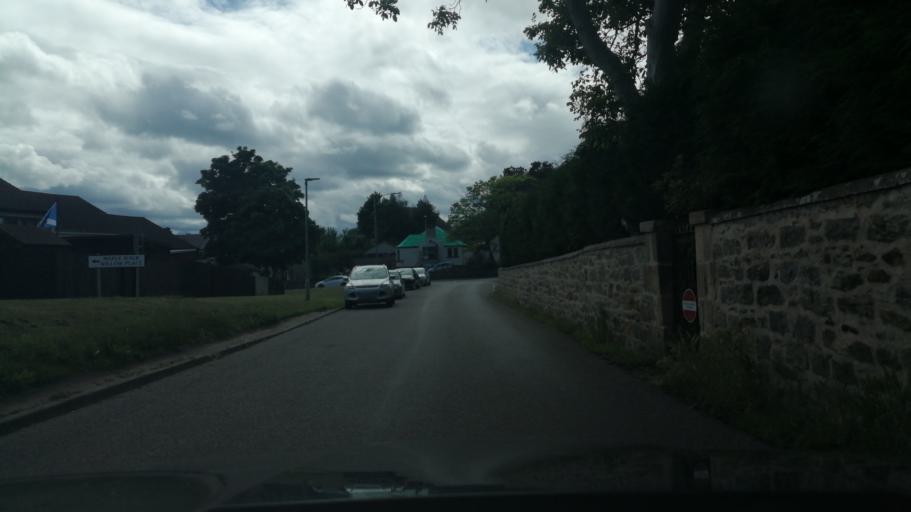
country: GB
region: Scotland
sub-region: Moray
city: Elgin
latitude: 57.6549
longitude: -3.2998
